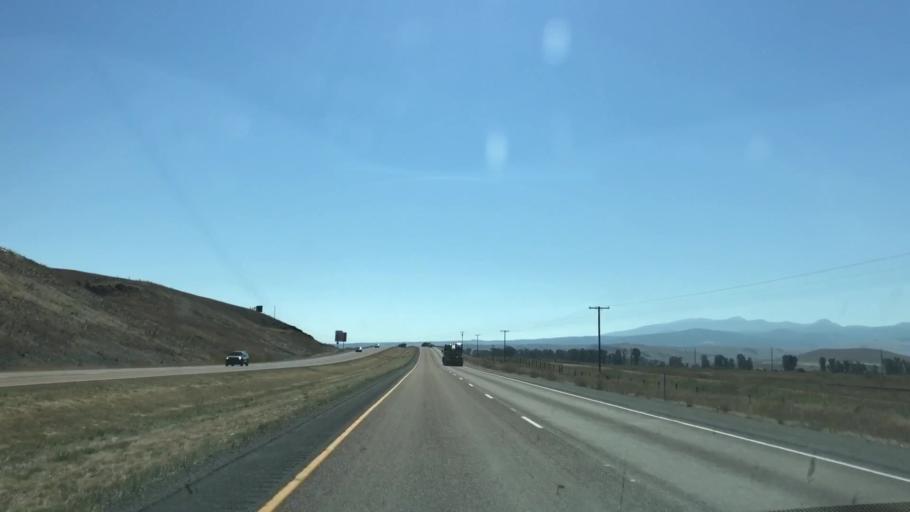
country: US
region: Montana
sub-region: Granite County
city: Philipsburg
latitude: 46.6525
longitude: -113.1232
